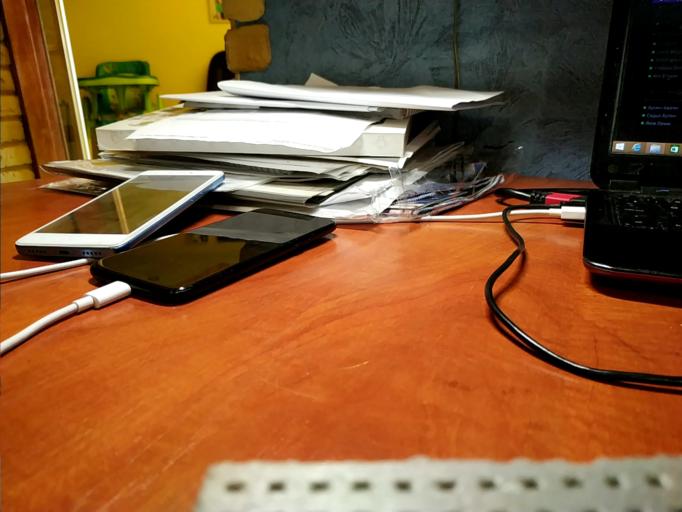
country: RU
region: Tverskaya
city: Spirovo
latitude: 57.4160
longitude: 35.1353
